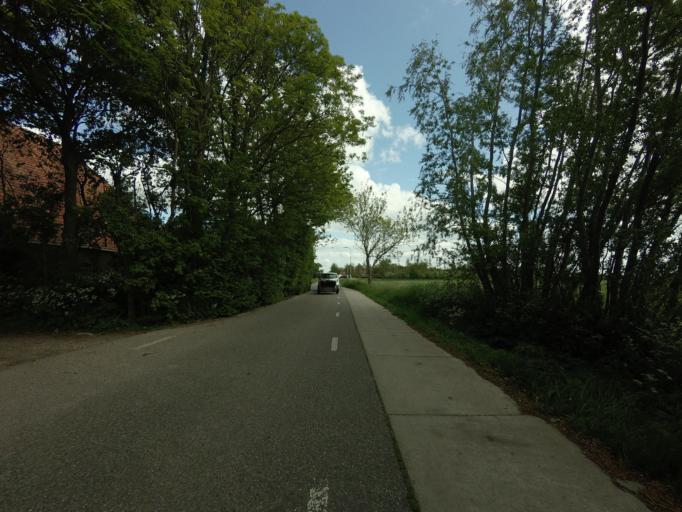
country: NL
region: Friesland
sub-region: Sudwest Fryslan
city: Bolsward
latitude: 53.0902
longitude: 5.5421
